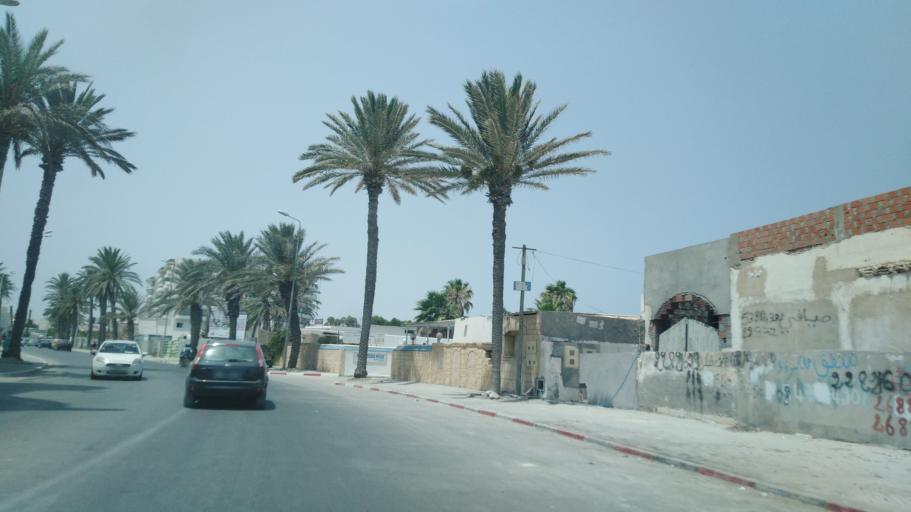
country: TN
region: Al Mahdiyah
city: Mahdia
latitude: 35.5114
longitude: 11.0524
